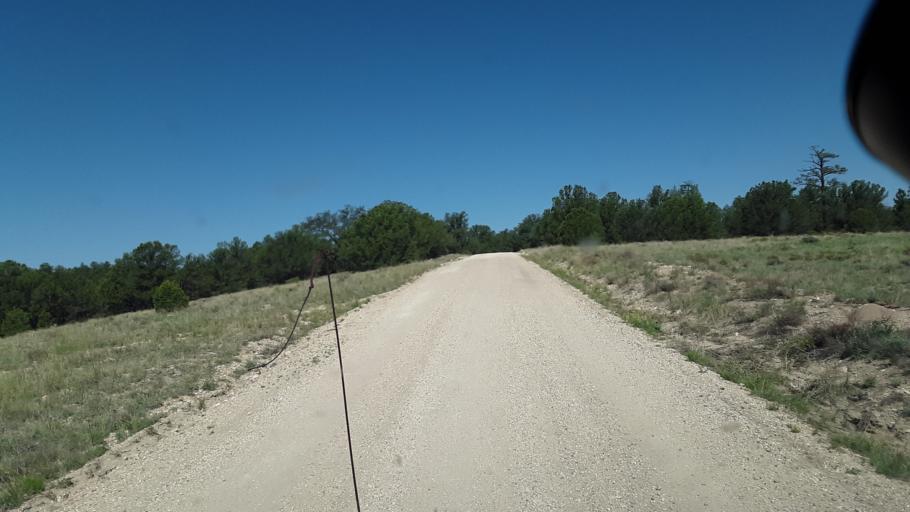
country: US
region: Colorado
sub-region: Custer County
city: Westcliffe
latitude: 38.2887
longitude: -105.4528
